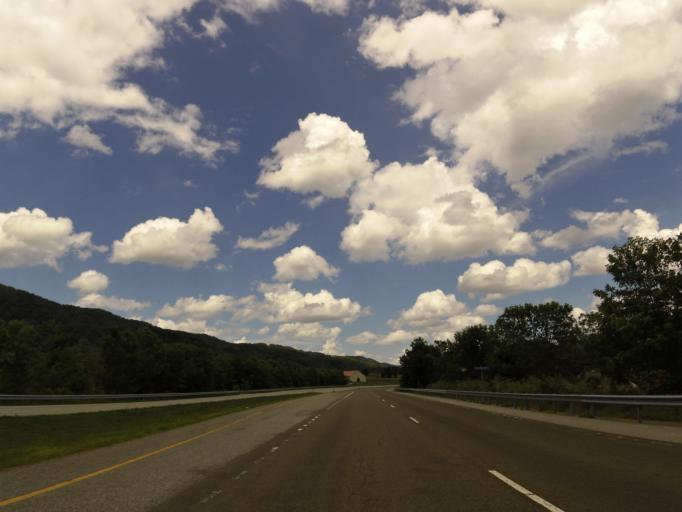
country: US
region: Kentucky
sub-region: Harlan County
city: Loyall
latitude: 36.6576
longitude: -83.3974
